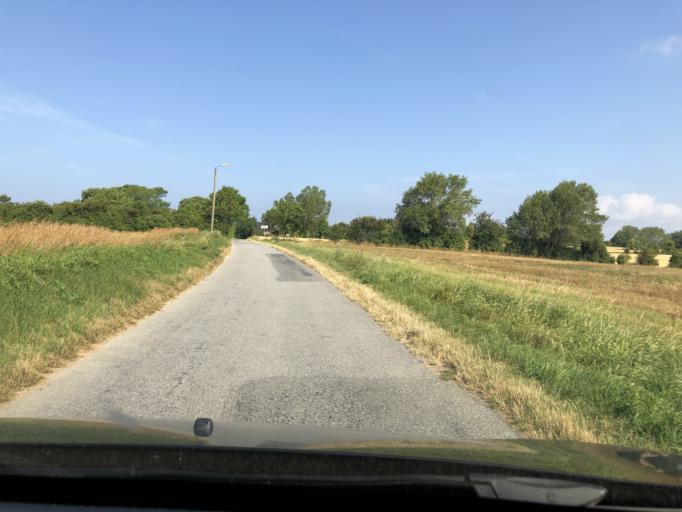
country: DK
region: South Denmark
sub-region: Faaborg-Midtfyn Kommune
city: Faaborg
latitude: 54.9529
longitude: 10.2272
